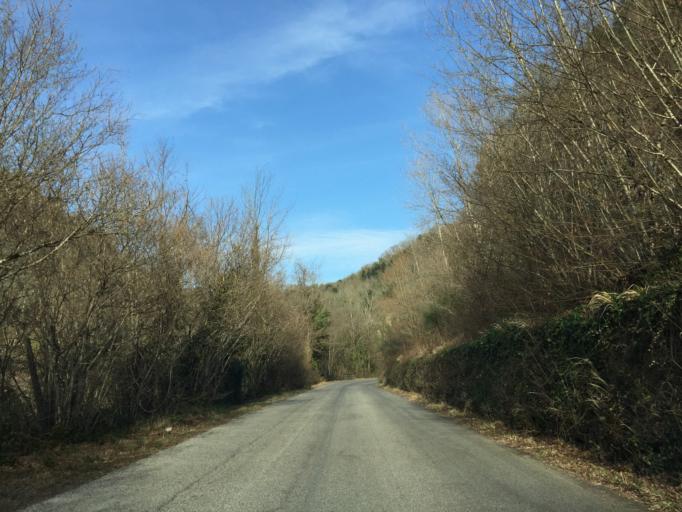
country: IT
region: Latium
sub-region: Provincia di Viterbo
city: Calcata Nuova
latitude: 42.2103
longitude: 12.4198
